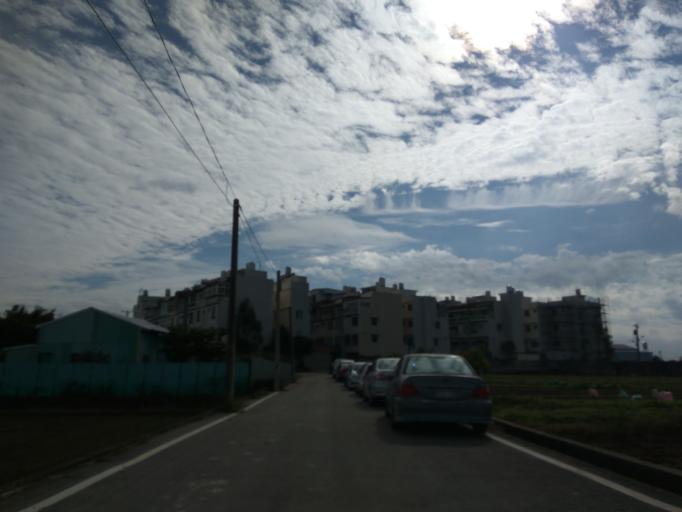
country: TW
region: Taiwan
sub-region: Hsinchu
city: Zhubei
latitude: 24.9881
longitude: 121.0927
